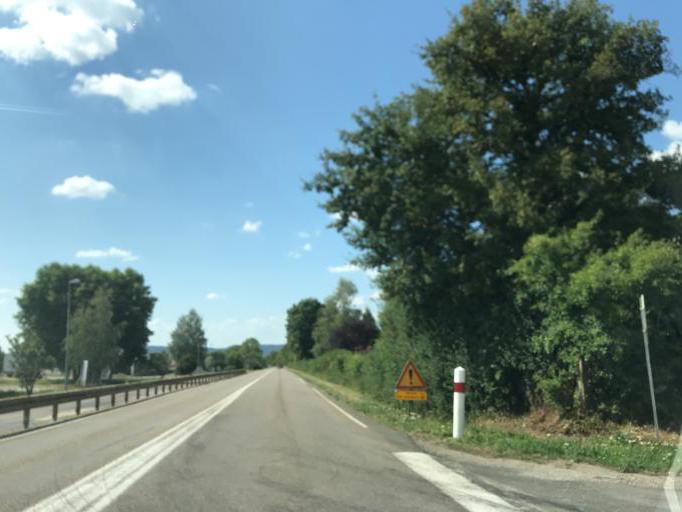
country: FR
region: Franche-Comte
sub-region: Departement du Jura
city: Clairvaux-les-Lacs
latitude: 46.5845
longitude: 5.7432
